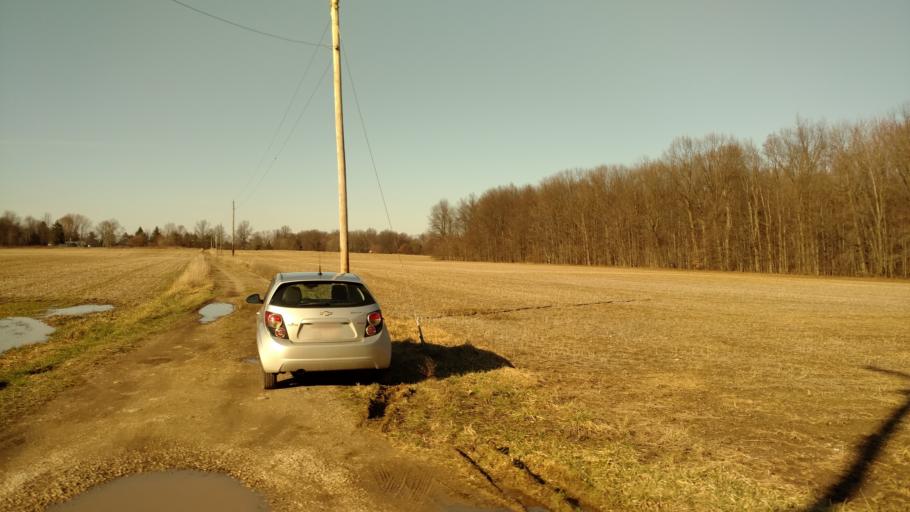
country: US
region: Ohio
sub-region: Crawford County
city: Galion
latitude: 40.6979
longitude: -82.8043
